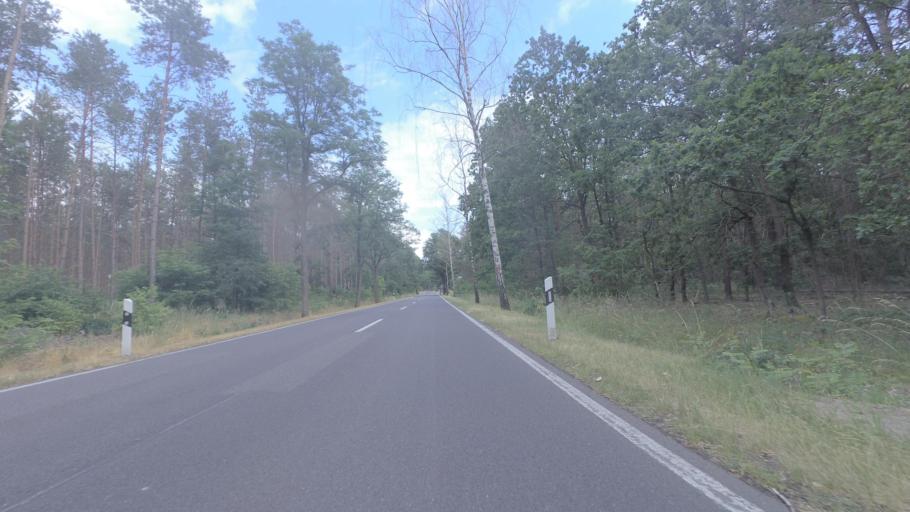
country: DE
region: Brandenburg
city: Am Mellensee
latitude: 52.1341
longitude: 13.4580
